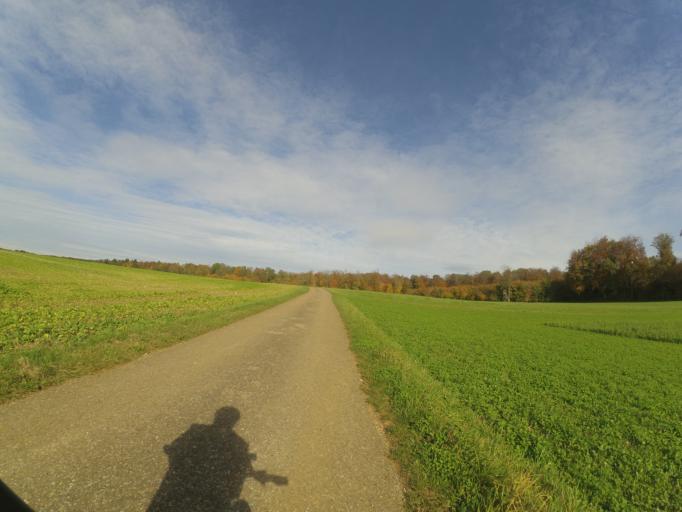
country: DE
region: Baden-Wuerttemberg
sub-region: Tuebingen Region
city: Amstetten
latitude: 48.6013
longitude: 9.9186
